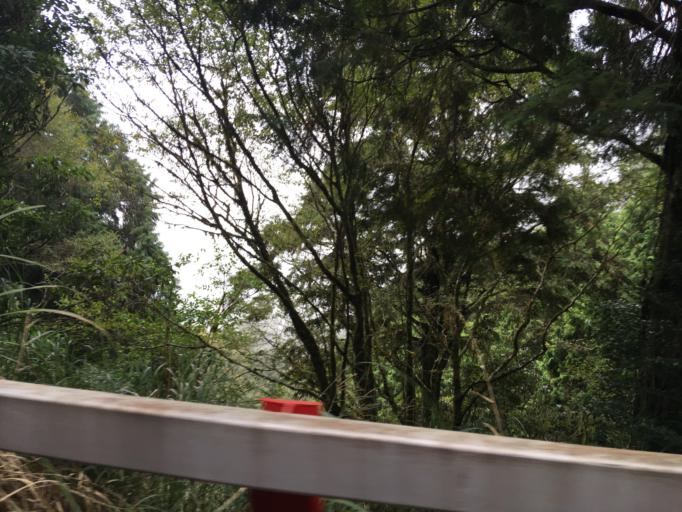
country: TW
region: Taiwan
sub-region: Yilan
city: Yilan
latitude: 24.4859
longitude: 121.5343
